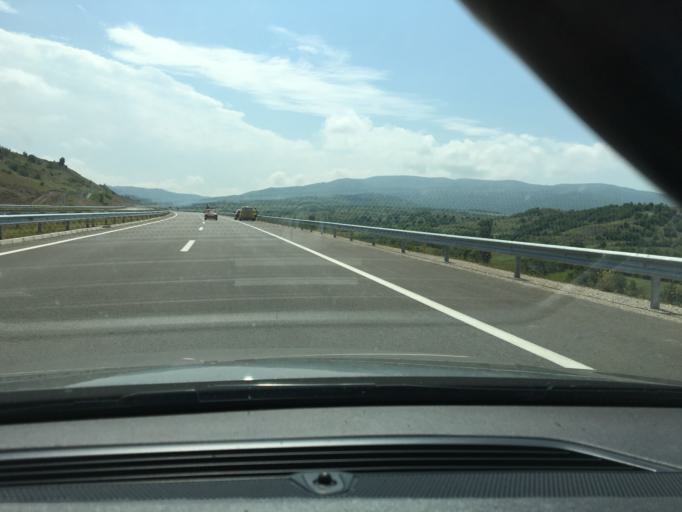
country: MK
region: Petrovec
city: Sredno Konjare
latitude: 41.9575
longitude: 21.7276
